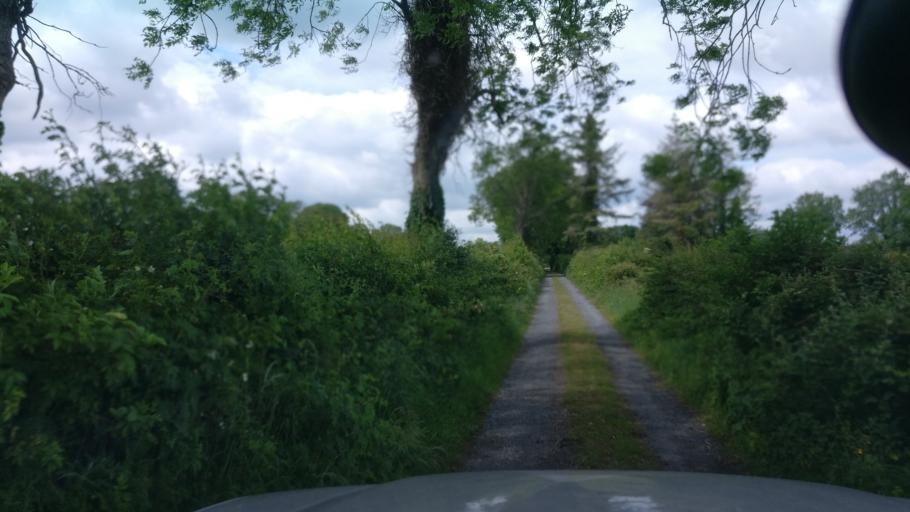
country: IE
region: Connaught
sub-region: County Galway
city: Ballinasloe
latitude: 53.2685
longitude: -8.3316
